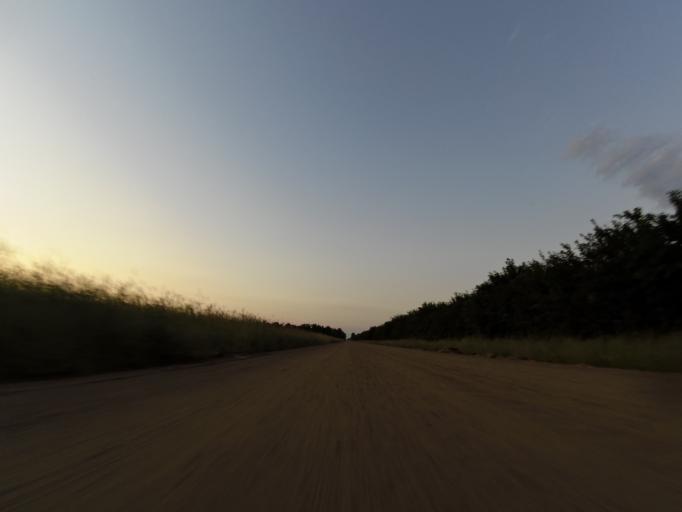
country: US
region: Kansas
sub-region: Reno County
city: South Hutchinson
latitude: 37.9640
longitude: -98.0320
